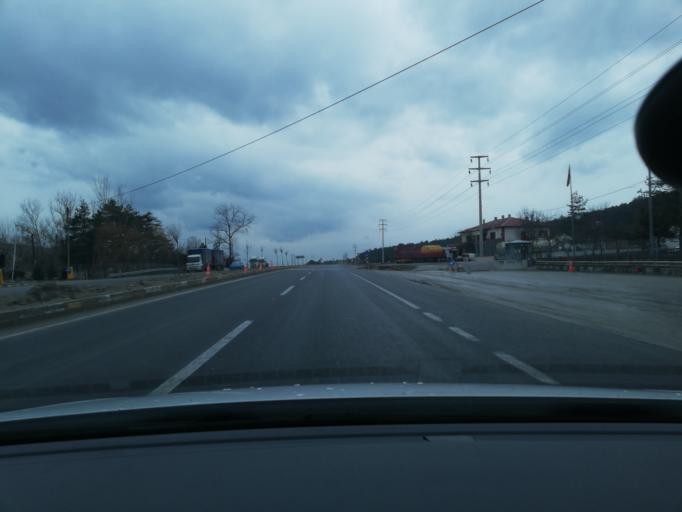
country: TR
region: Bolu
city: Yenicaga
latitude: 40.7575
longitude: 31.9219
